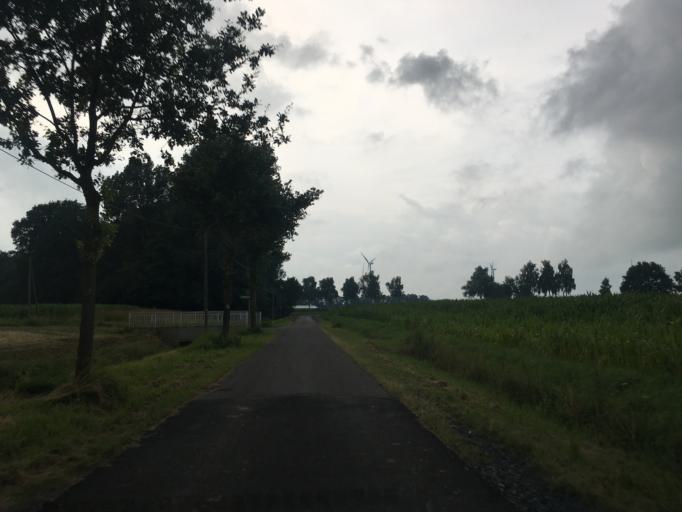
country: DE
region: North Rhine-Westphalia
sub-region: Regierungsbezirk Munster
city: Greven
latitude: 52.0415
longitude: 7.6052
